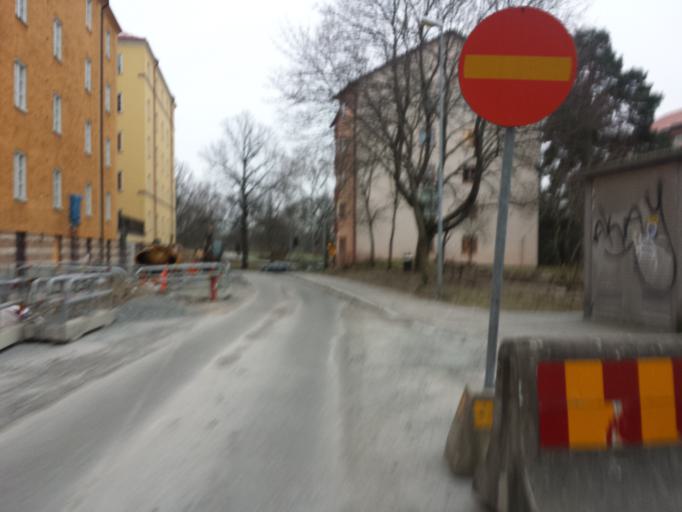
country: SE
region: Stockholm
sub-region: Solna Kommun
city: Solna
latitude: 59.3627
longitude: 18.0204
